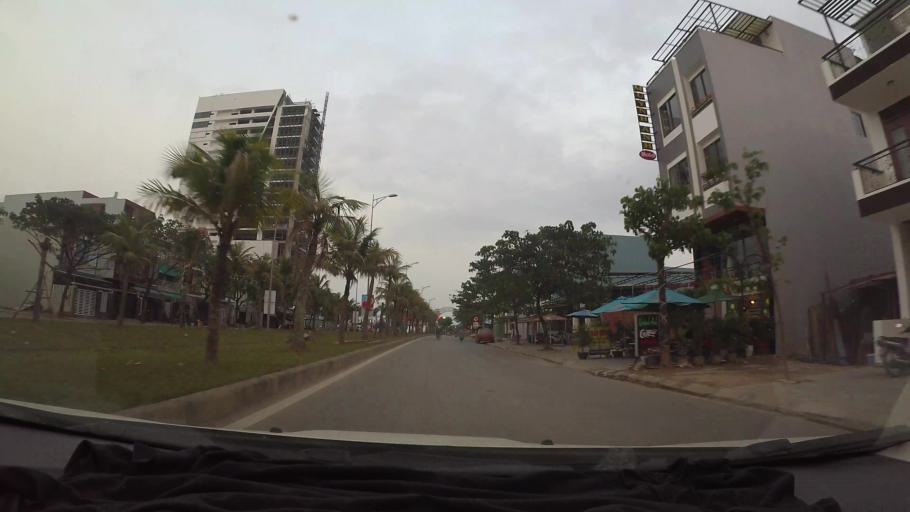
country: VN
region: Da Nang
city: Lien Chieu
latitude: 16.1085
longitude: 108.1292
